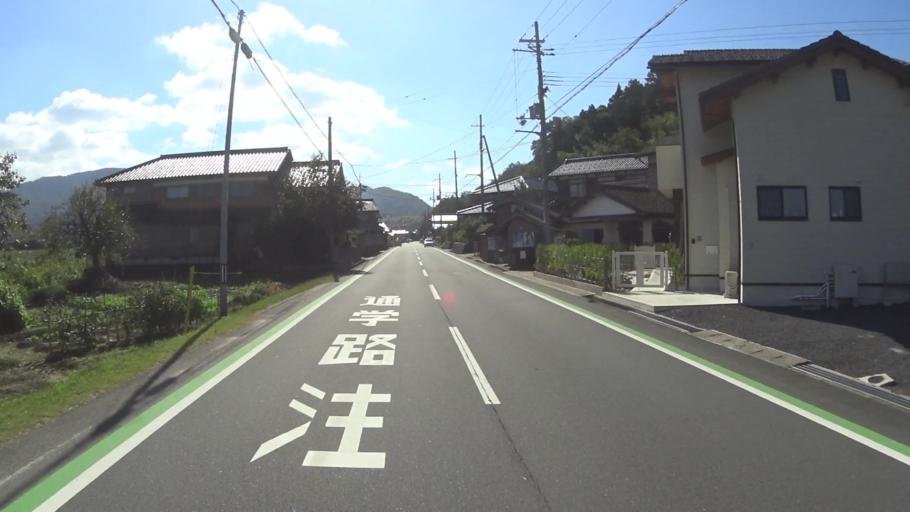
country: JP
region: Kyoto
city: Miyazu
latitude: 35.6574
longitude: 135.0884
